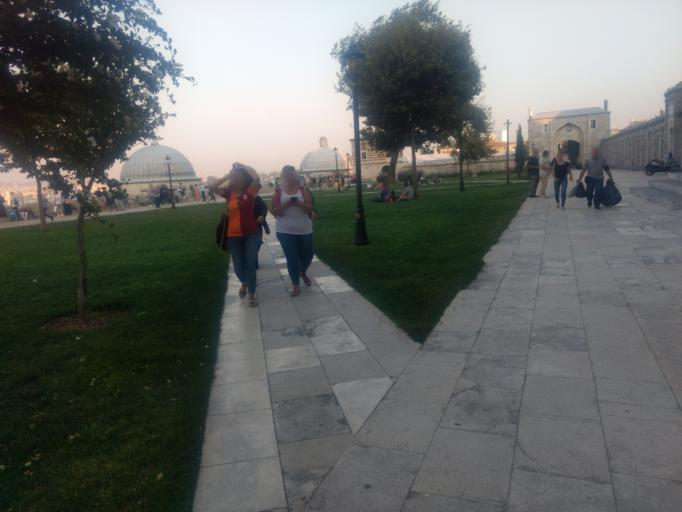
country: TR
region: Istanbul
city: Eminoenue
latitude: 41.0163
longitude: 28.9644
